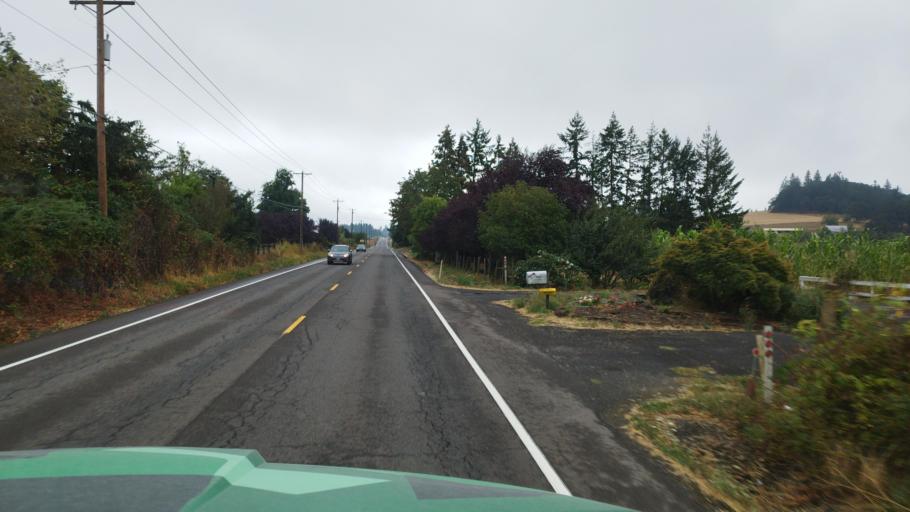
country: US
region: Oregon
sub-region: Yamhill County
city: Yamhill
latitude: 45.3294
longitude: -123.1829
